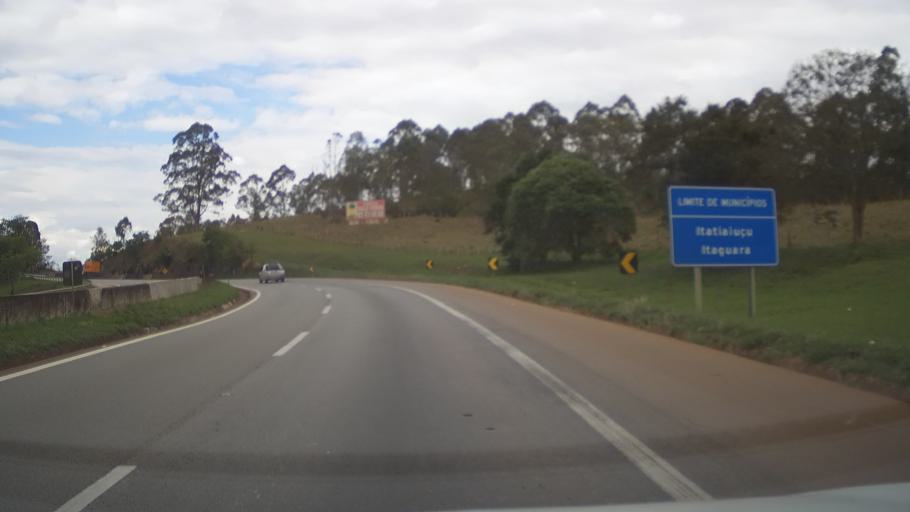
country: BR
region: Minas Gerais
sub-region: Itauna
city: Itauna
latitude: -20.3006
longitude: -44.4420
